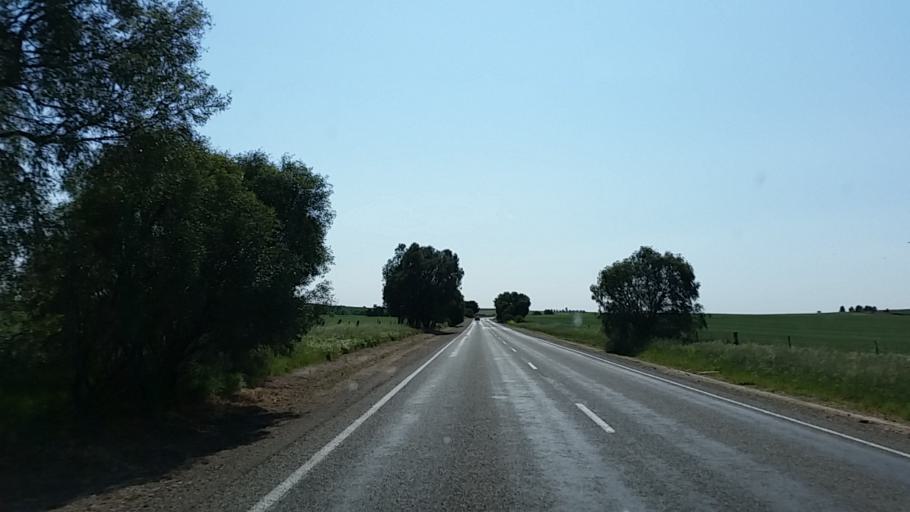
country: AU
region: South Australia
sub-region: Northern Areas
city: Jamestown
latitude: -33.2189
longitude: 138.4136
